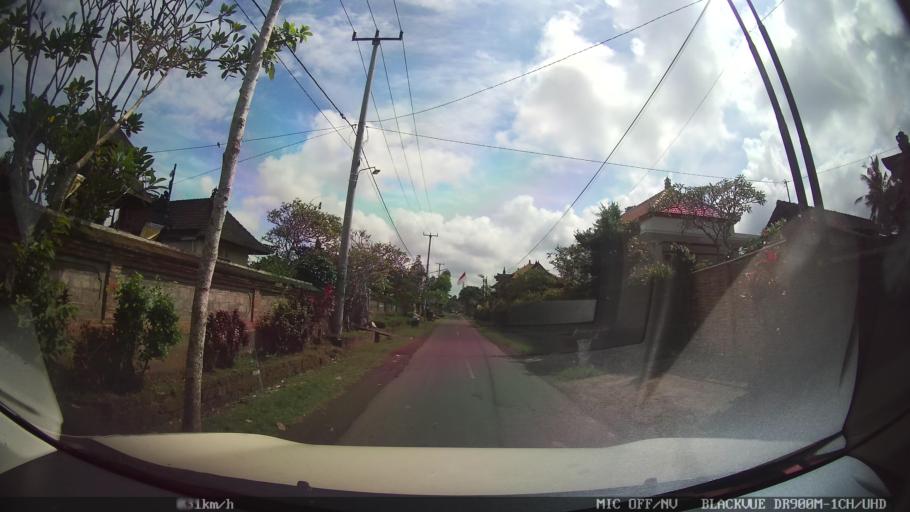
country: ID
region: Bali
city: Banjar Tebongkang
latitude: -8.5373
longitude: 115.2521
